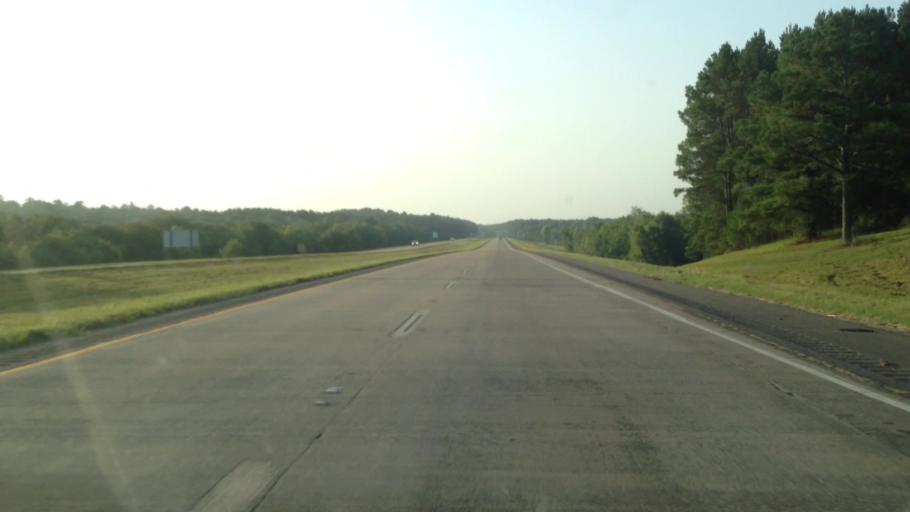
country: US
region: Louisiana
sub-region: Grant Parish
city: Colfax
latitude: 31.4891
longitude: -92.8545
